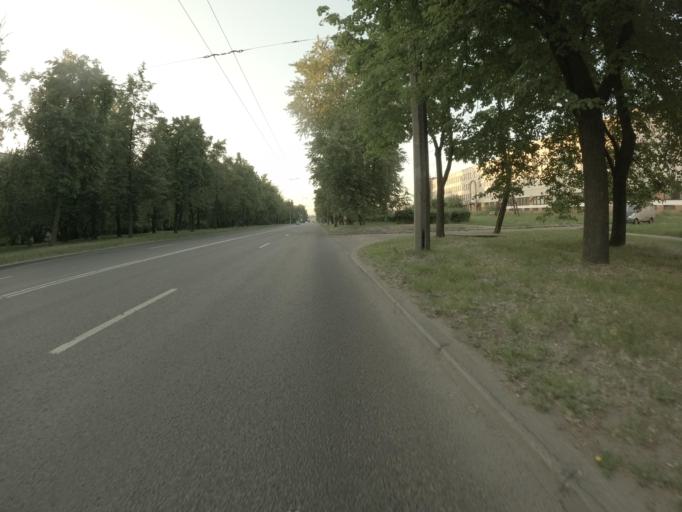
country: RU
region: St.-Petersburg
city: Avtovo
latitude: 59.8742
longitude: 30.2756
